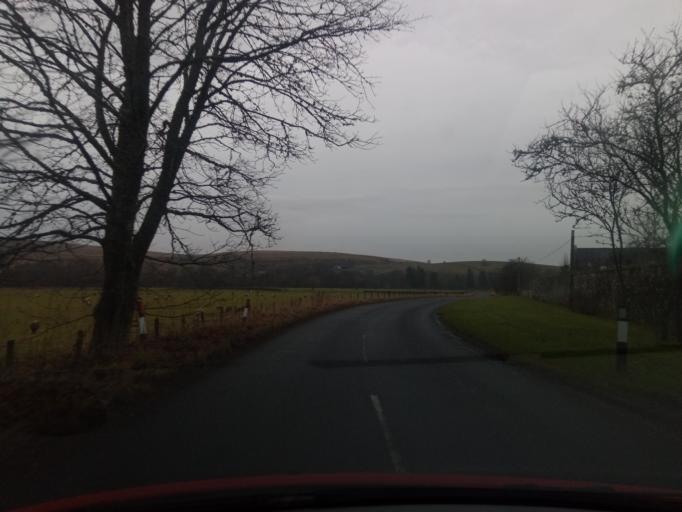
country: GB
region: England
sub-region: Northumberland
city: Rochester
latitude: 55.1669
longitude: -2.3610
